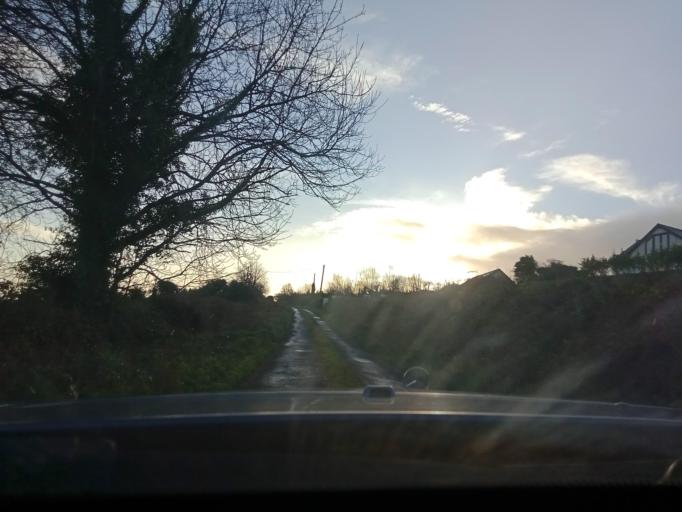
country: IE
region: Leinster
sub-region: Kilkenny
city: Callan
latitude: 52.4696
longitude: -7.4246
